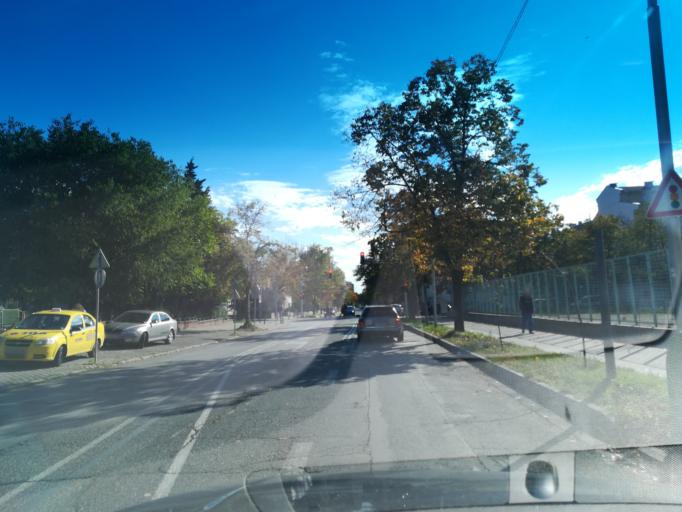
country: BG
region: Stara Zagora
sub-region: Obshtina Stara Zagora
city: Stara Zagora
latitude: 42.4309
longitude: 25.6397
